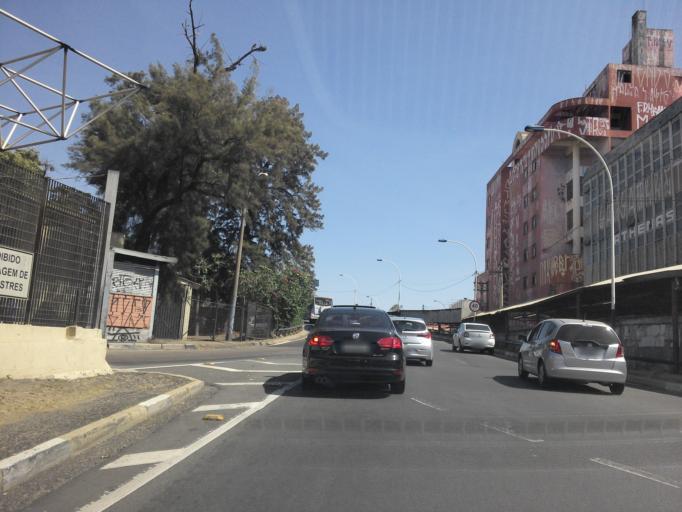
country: BR
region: Sao Paulo
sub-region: Campinas
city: Campinas
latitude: -22.9087
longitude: -47.0628
